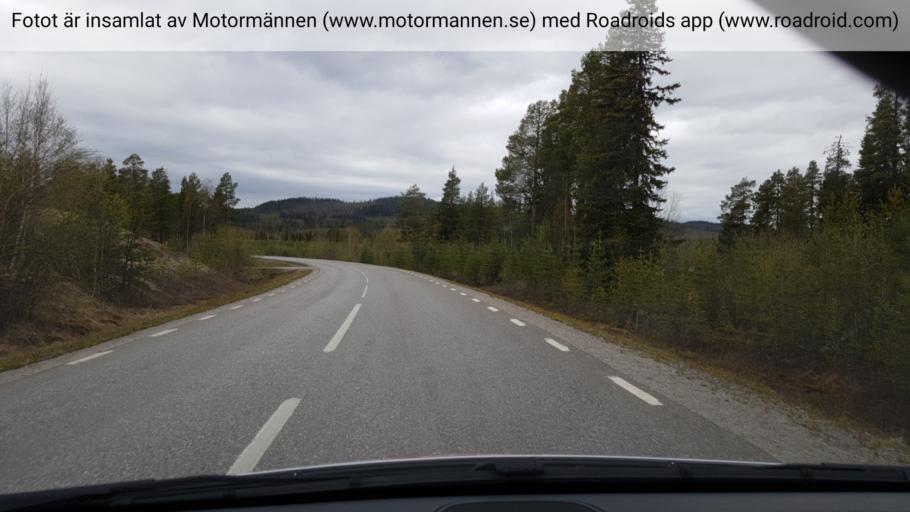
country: SE
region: Vaesterbotten
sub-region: Sorsele Kommun
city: Sorsele
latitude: 65.5519
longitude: 17.4931
